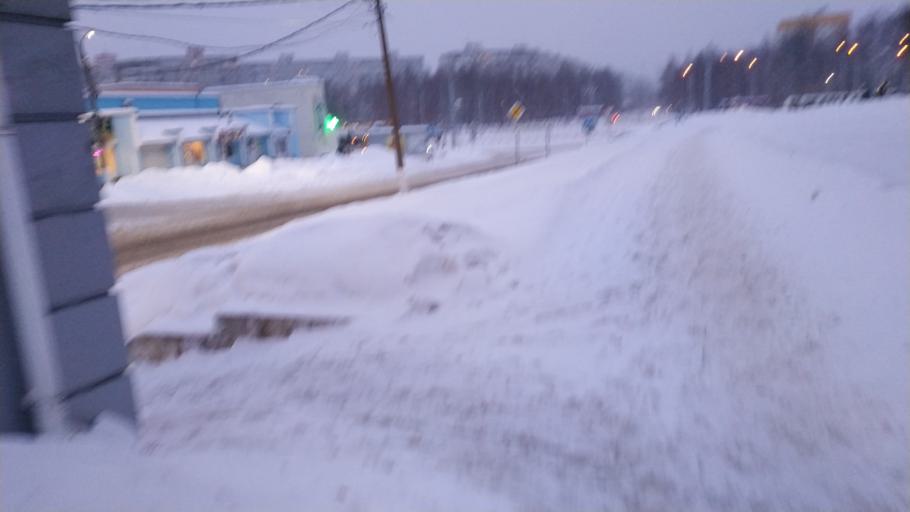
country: RU
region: Moskovskaya
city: Sychevo
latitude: 55.0551
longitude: 38.7474
